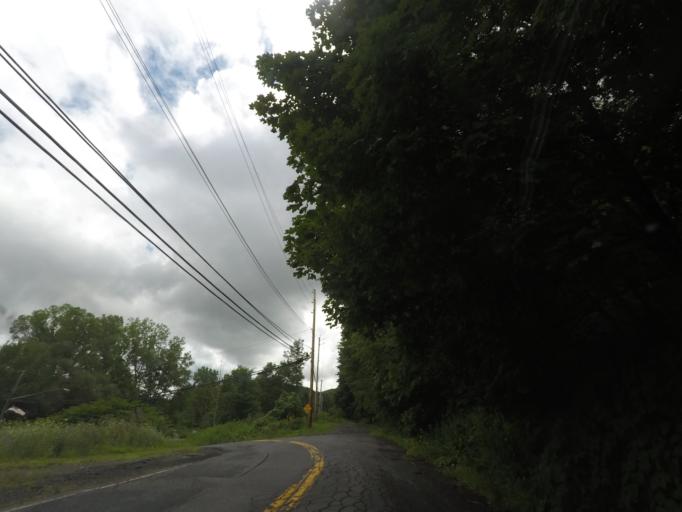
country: US
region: Massachusetts
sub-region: Berkshire County
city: Williamstown
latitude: 42.6896
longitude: -73.3701
